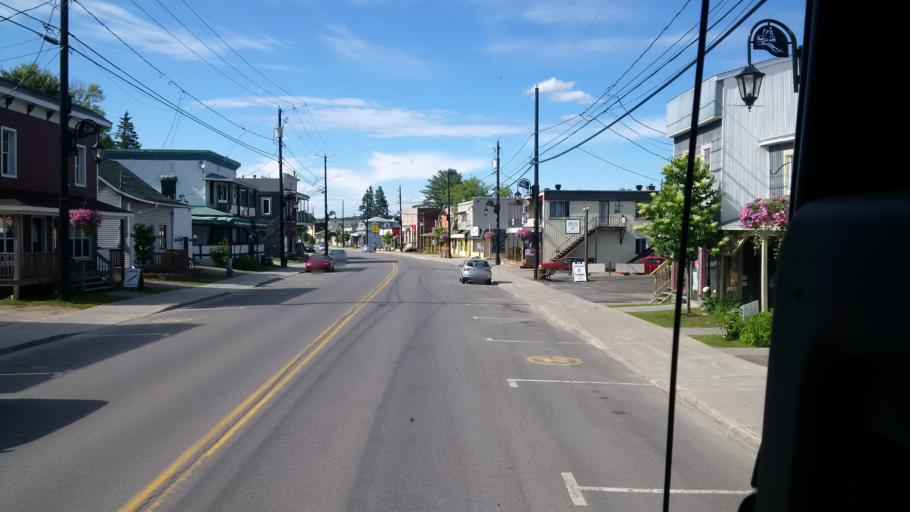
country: CA
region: Quebec
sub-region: Laurentides
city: Riviere-Rouge
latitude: 46.4112
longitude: -74.8704
